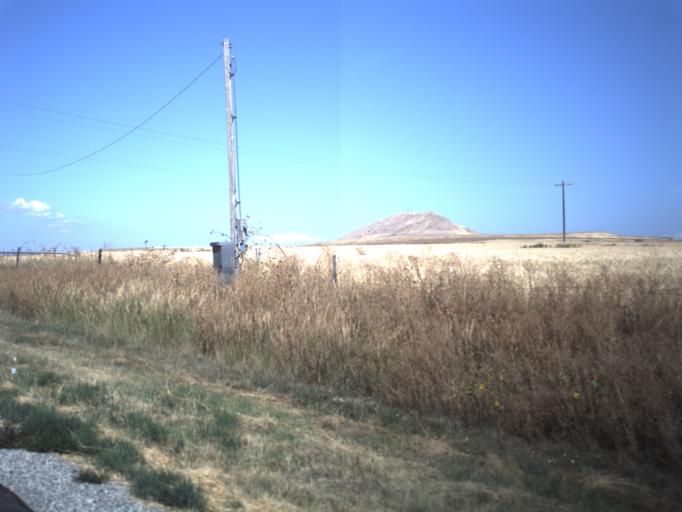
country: US
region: Utah
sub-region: Cache County
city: Benson
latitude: 41.8527
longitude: -111.9717
